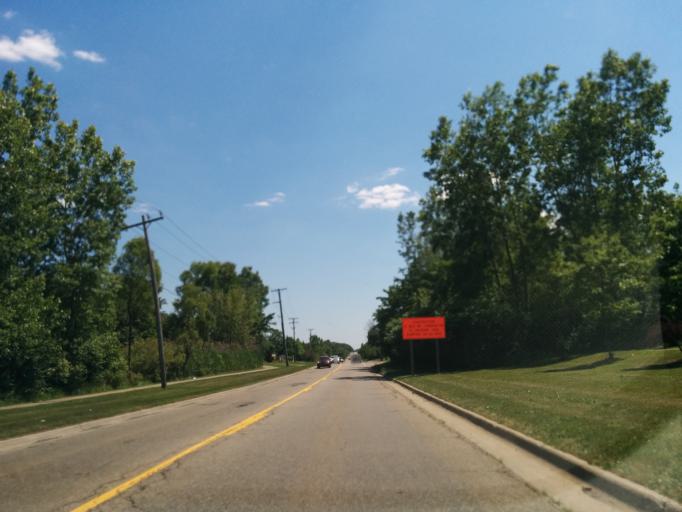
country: US
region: Michigan
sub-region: Oakland County
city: West Bloomfield Township
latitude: 42.5382
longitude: -83.3802
